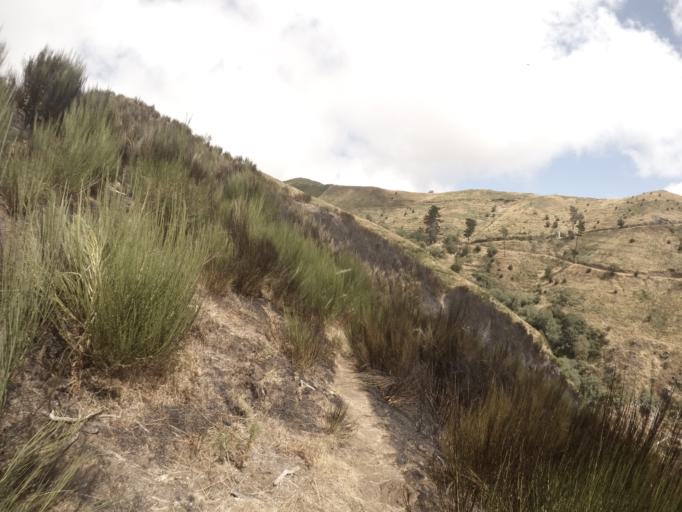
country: PT
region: Madeira
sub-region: Camara de Lobos
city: Curral das Freiras
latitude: 32.7098
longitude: -17.0021
